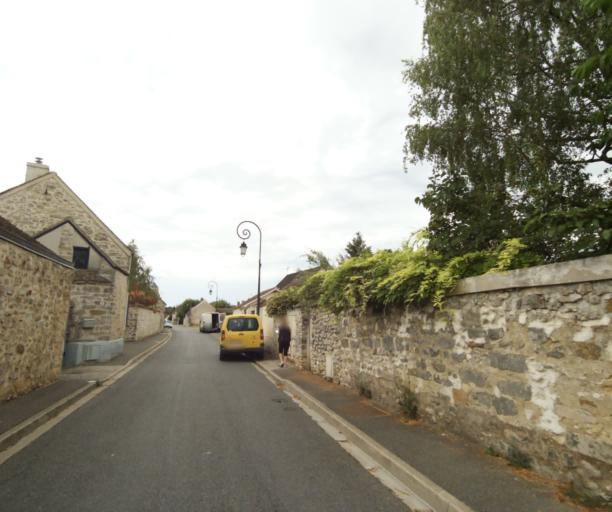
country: FR
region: Ile-de-France
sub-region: Departement de l'Essonne
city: Soisy-sur-Ecole
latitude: 48.4771
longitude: 2.4970
